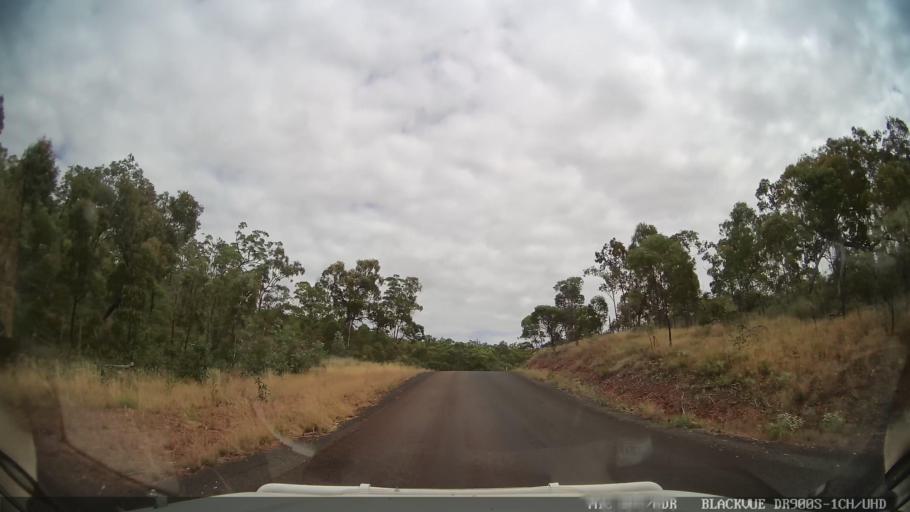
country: AU
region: Queensland
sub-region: Cook
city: Cooktown
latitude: -15.2827
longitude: 144.9107
